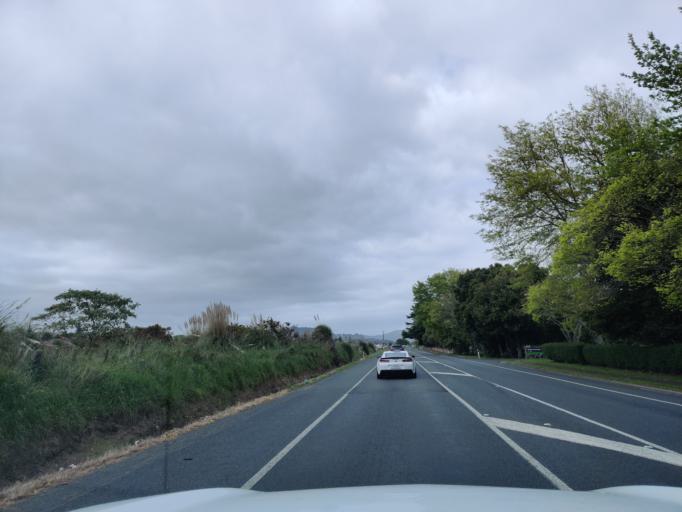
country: NZ
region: Waikato
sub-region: Waikato District
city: Te Kauwhata
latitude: -37.5301
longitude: 175.1592
